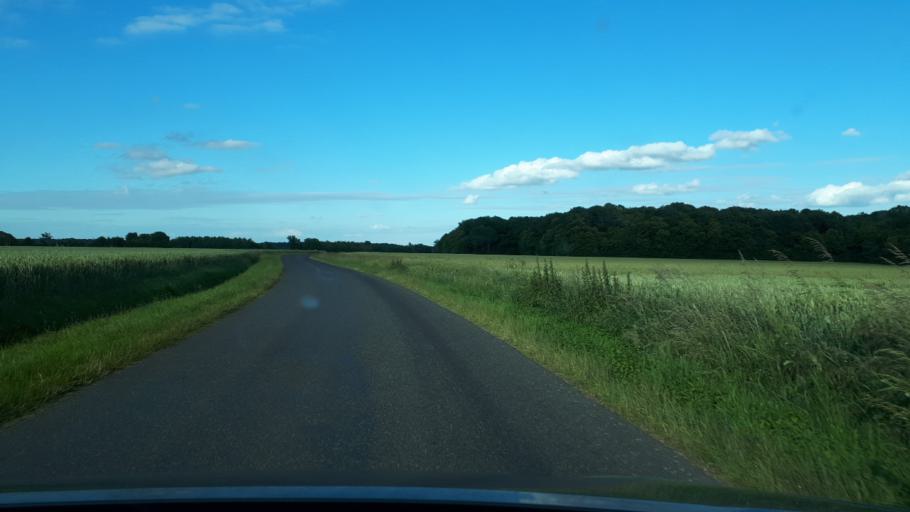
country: FR
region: Centre
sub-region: Departement du Loir-et-Cher
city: Sarge-sur-Braye
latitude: 47.9260
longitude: 0.8935
